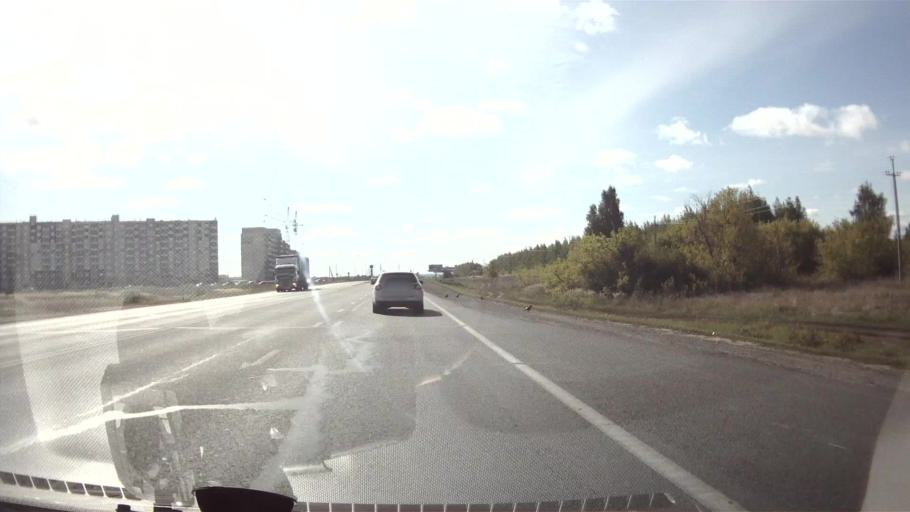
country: RU
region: Ulyanovsk
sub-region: Ulyanovskiy Rayon
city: Ulyanovsk
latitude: 54.2856
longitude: 48.2568
